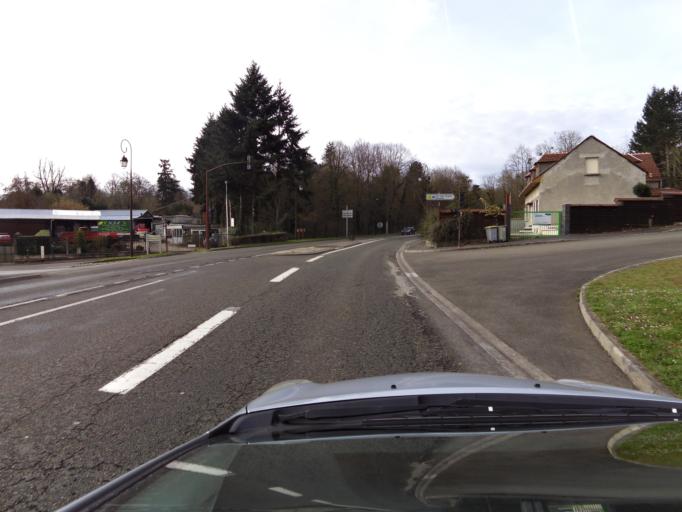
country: FR
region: Picardie
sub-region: Departement de l'Oise
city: Ver-sur-Launette
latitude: 49.1277
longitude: 2.6893
